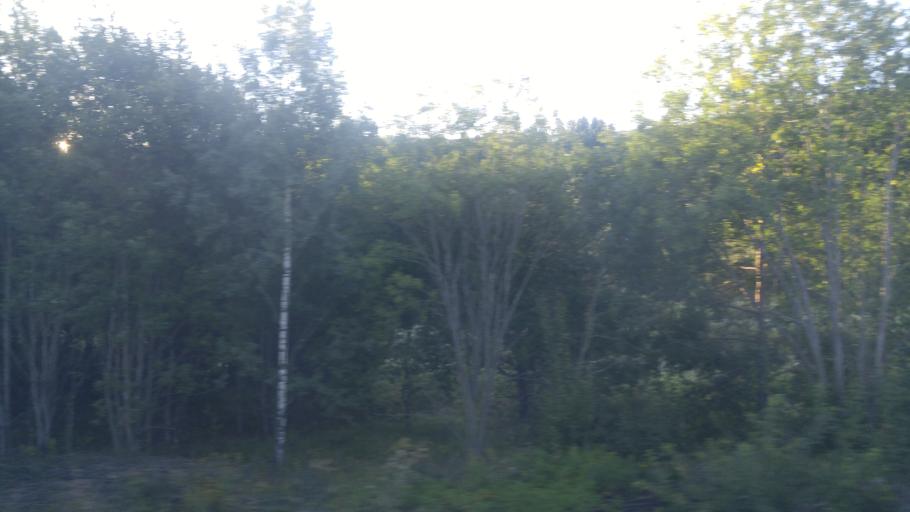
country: NO
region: Oslo
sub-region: Oslo
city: Oslo
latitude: 59.9165
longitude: 10.8294
